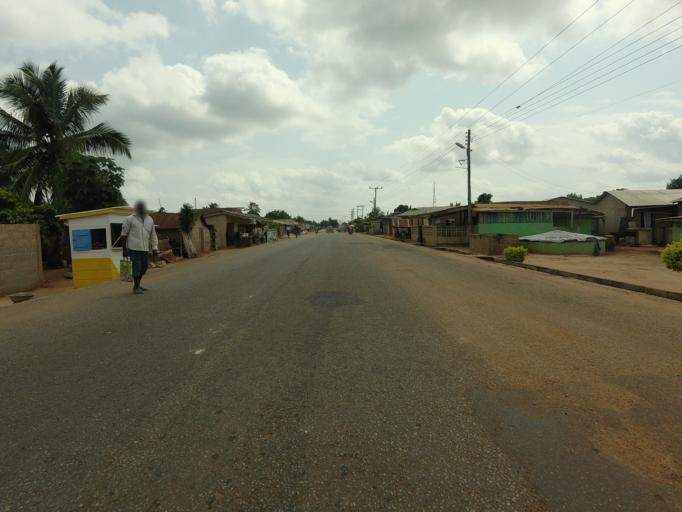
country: TG
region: Maritime
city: Lome
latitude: 6.2214
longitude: 1.0391
